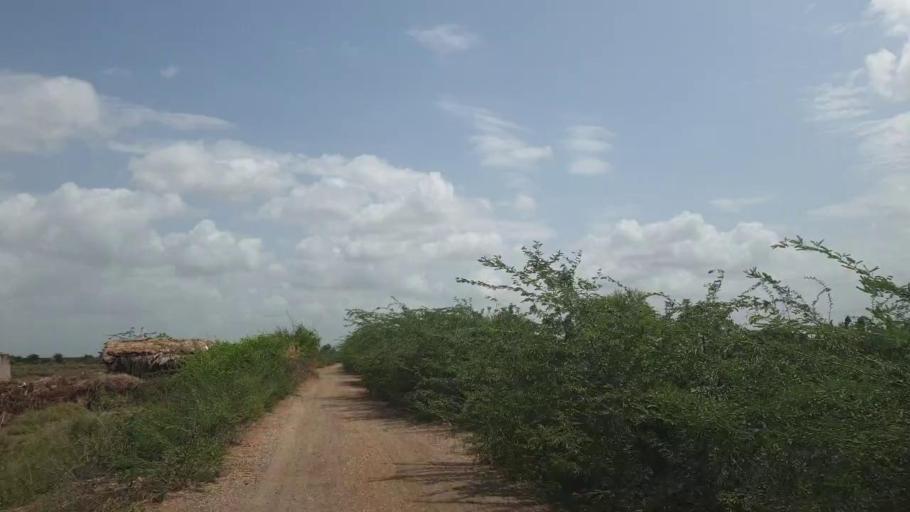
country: PK
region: Sindh
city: Tando Bago
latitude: 24.6546
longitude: 68.9928
